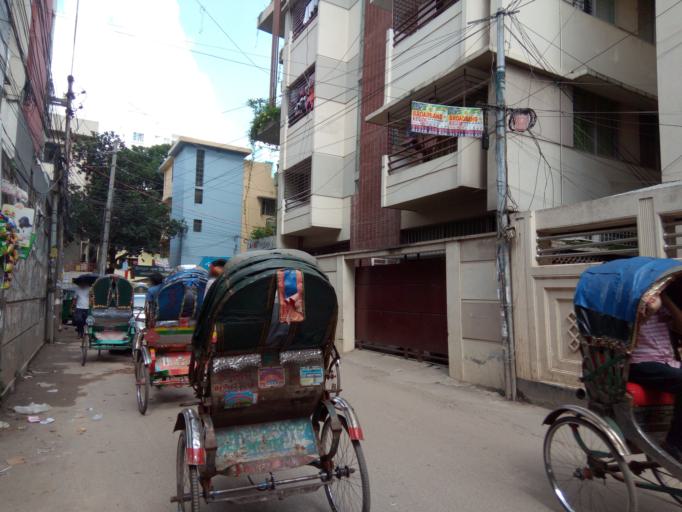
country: BD
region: Dhaka
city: Azimpur
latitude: 23.7416
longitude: 90.3873
